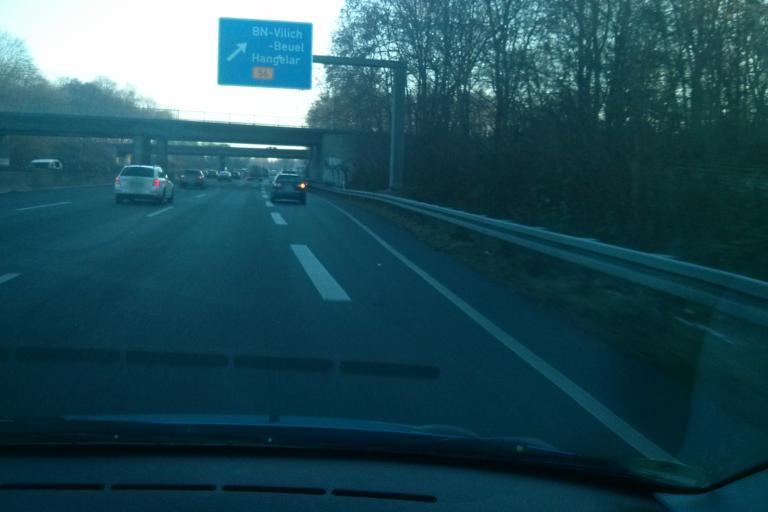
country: DE
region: North Rhine-Westphalia
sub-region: Regierungsbezirk Koln
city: Bonn
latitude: 50.7538
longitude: 7.1409
